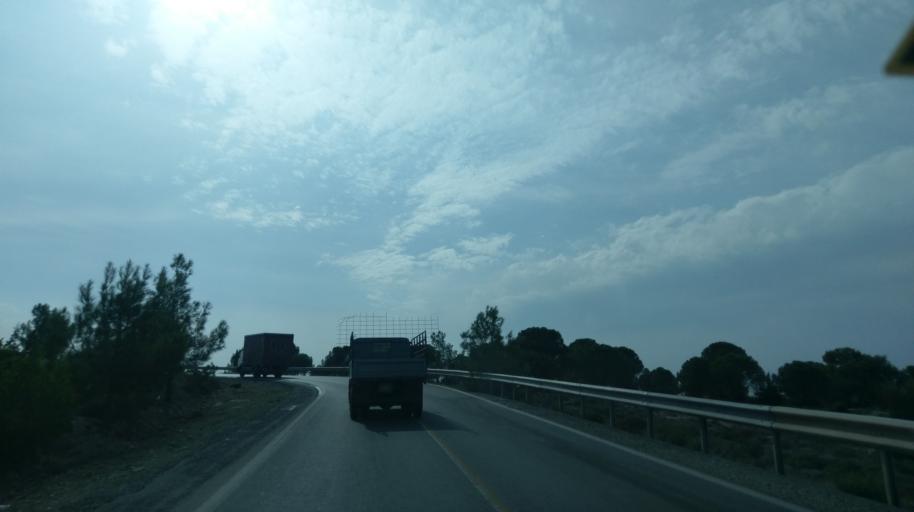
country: CY
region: Lefkosia
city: Morfou
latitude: 35.2525
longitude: 33.0323
